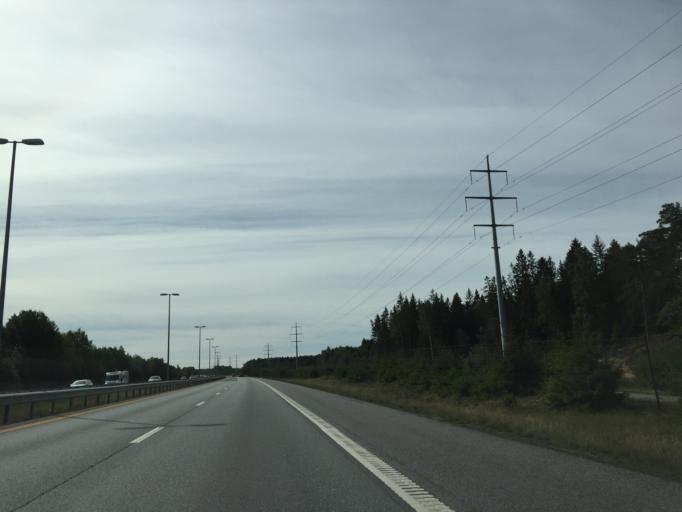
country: NO
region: Akershus
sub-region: Vestby
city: Vestby
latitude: 59.5623
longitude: 10.7208
